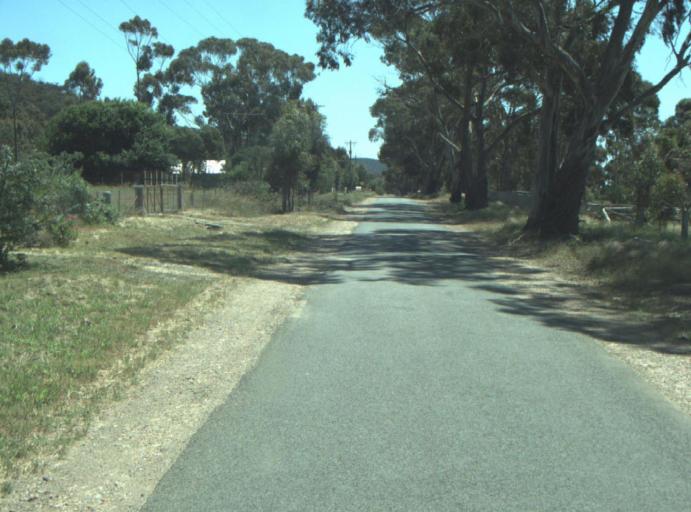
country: AU
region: Victoria
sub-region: Greater Geelong
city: Lara
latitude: -37.8459
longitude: 144.2824
